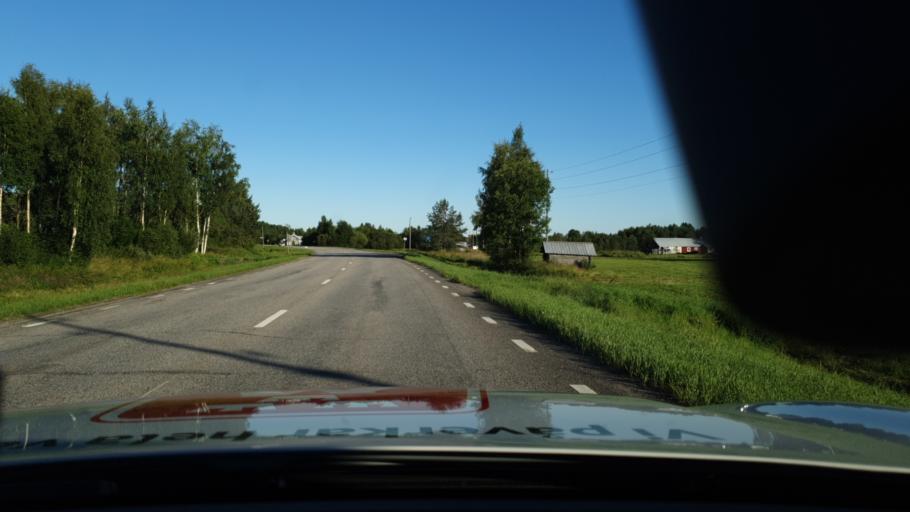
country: SE
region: Norrbotten
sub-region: Pitea Kommun
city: Rosvik
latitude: 65.5662
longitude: 21.7789
